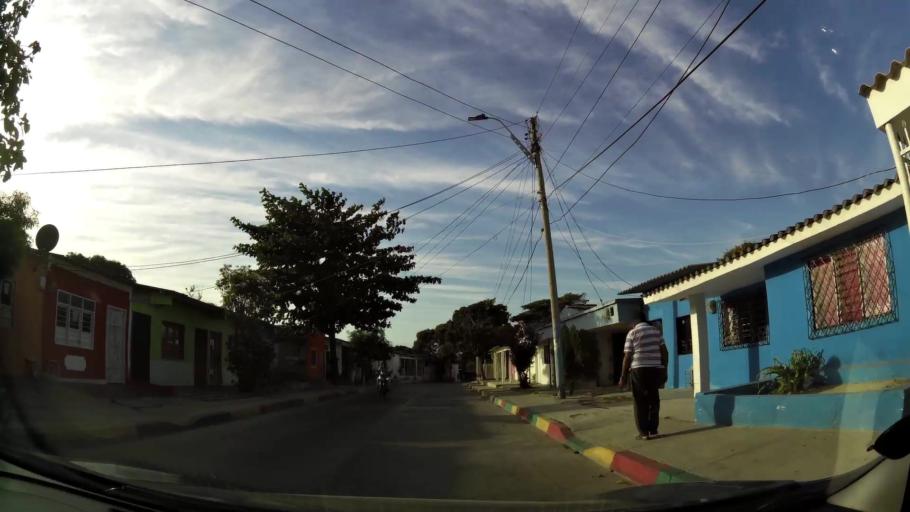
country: CO
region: Atlantico
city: Barranquilla
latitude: 10.9427
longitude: -74.8204
